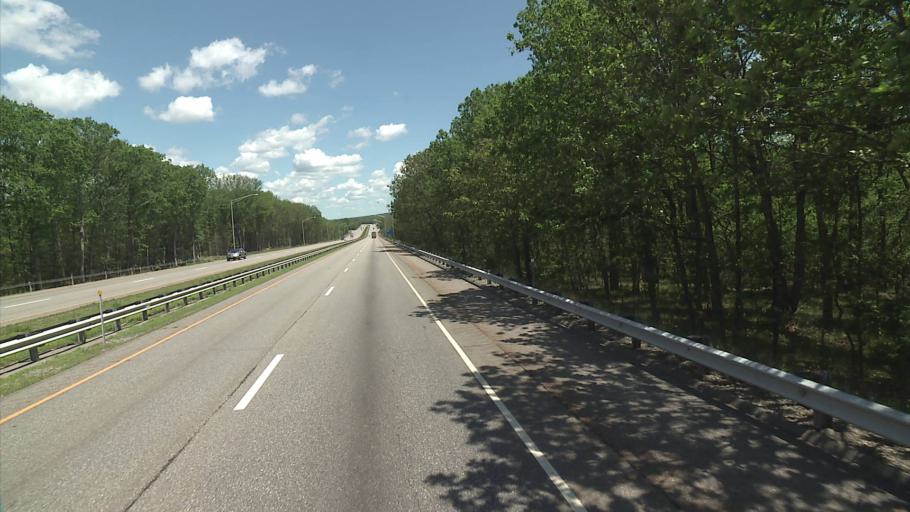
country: US
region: Connecticut
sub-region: Windham County
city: Plainfield Village
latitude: 41.6589
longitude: -71.9210
